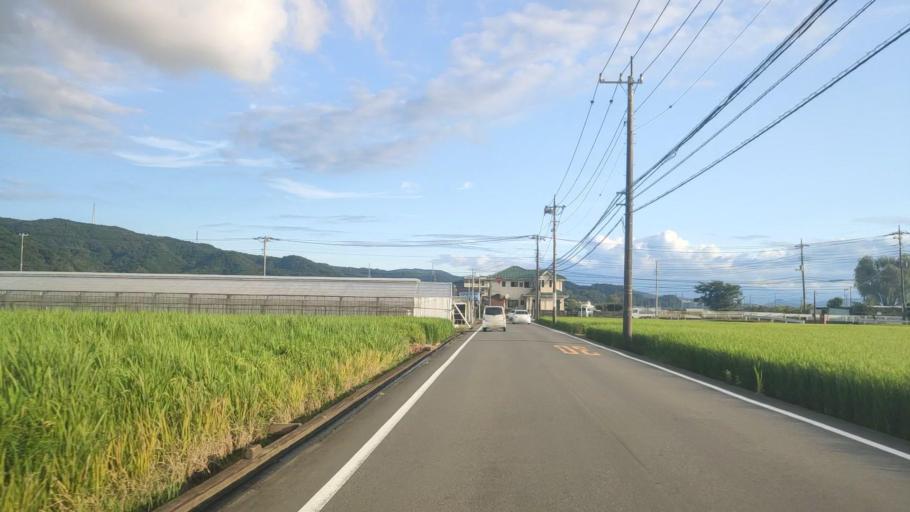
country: JP
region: Shizuoka
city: Mishima
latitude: 35.0673
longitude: 138.9522
